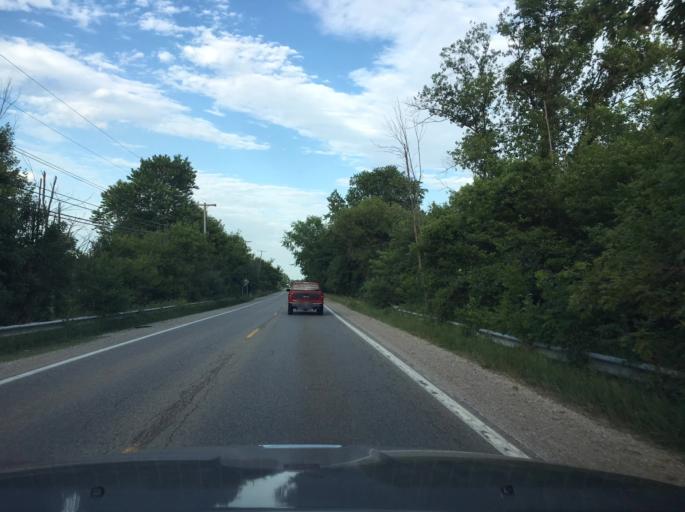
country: US
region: Michigan
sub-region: Macomb County
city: New Haven
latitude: 42.7172
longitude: -82.9038
